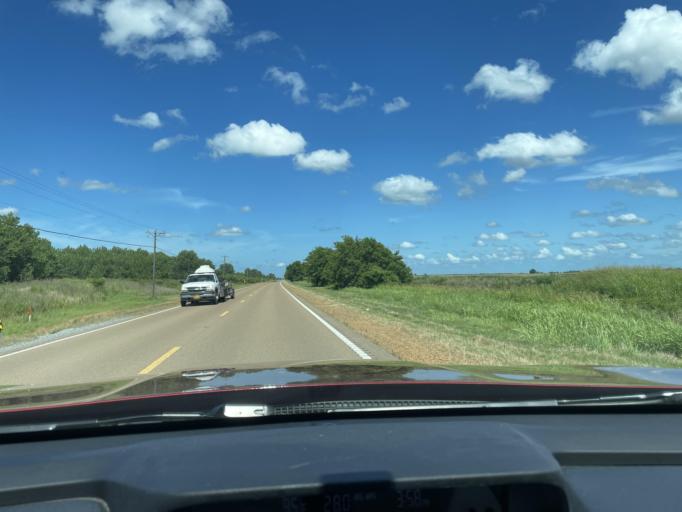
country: US
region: Mississippi
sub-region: Humphreys County
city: Belzoni
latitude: 33.1836
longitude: -90.5924
